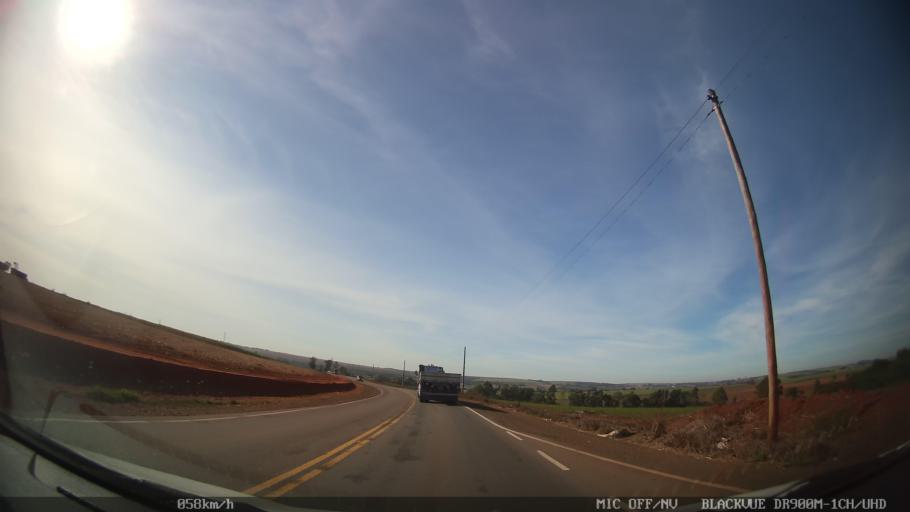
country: BR
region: Sao Paulo
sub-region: Piracicaba
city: Piracicaba
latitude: -22.7899
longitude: -47.6447
